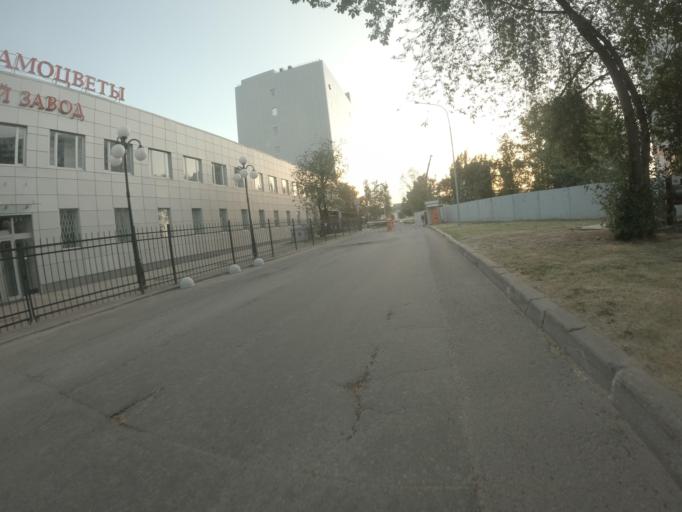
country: RU
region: St.-Petersburg
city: Krasnogvargeisky
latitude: 59.9357
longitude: 30.4383
